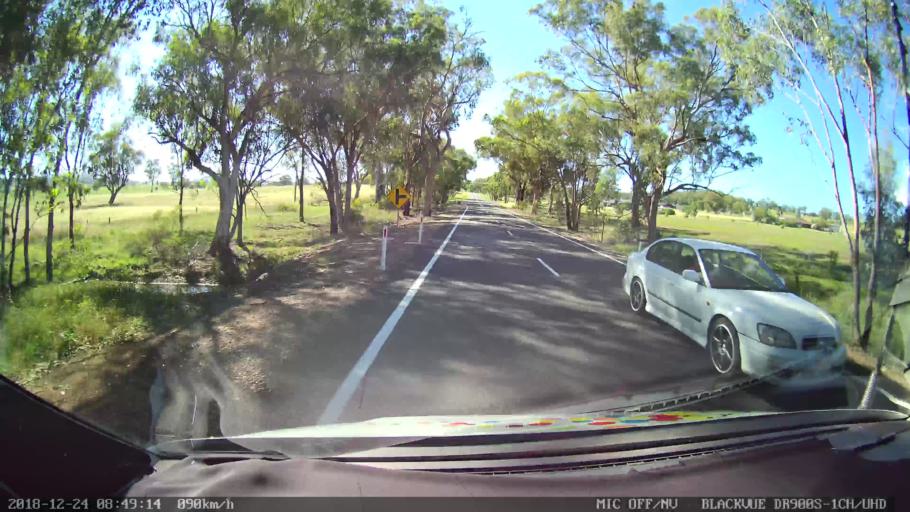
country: AU
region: New South Wales
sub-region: Liverpool Plains
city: Quirindi
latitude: -31.4651
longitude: 150.6520
